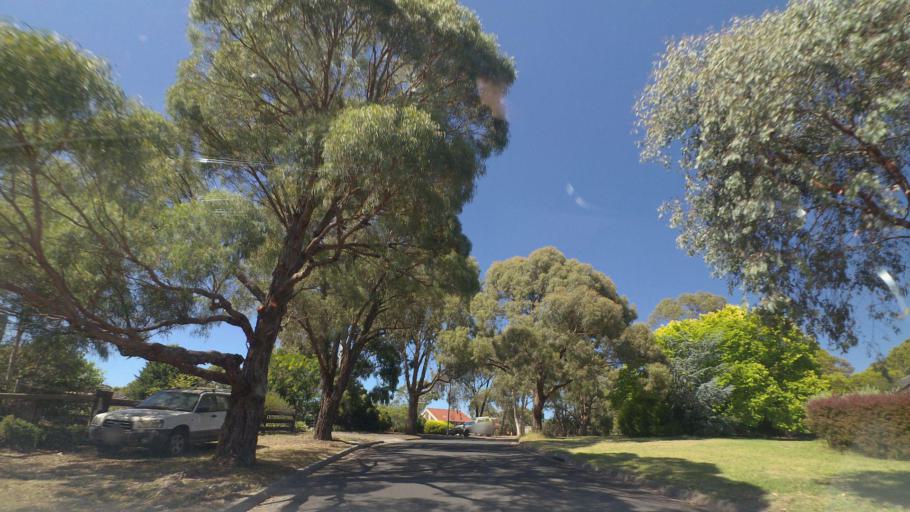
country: AU
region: Victoria
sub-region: Manningham
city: Park Orchards
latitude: -37.7716
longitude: 145.2255
